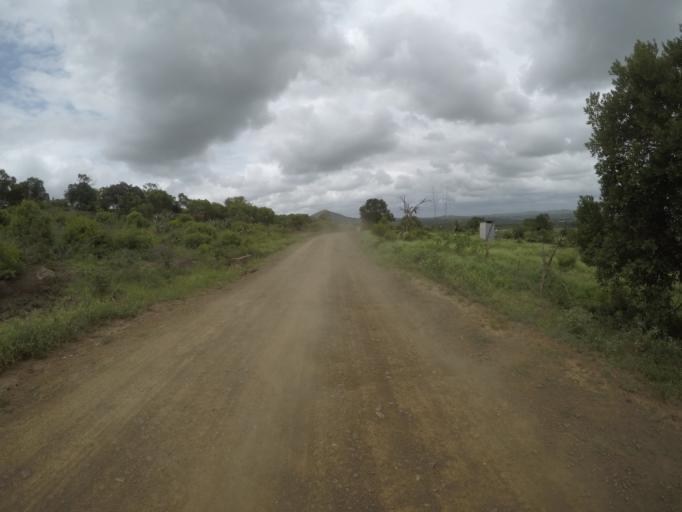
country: ZA
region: KwaZulu-Natal
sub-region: uThungulu District Municipality
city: Empangeni
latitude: -28.5793
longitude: 31.8676
